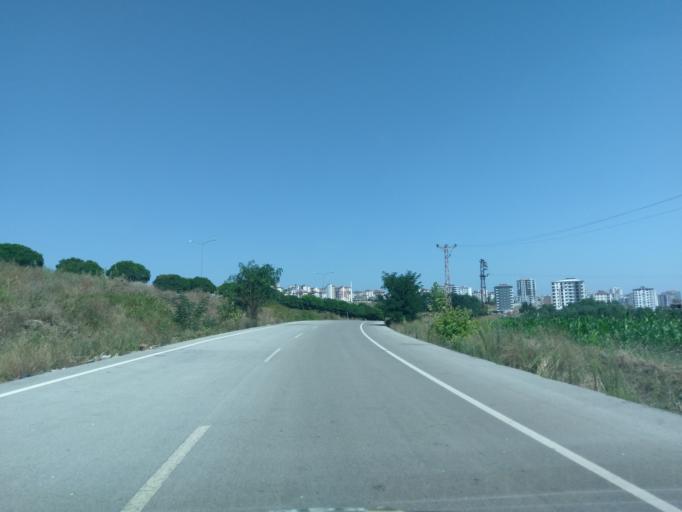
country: TR
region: Samsun
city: Samsun
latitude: 41.2579
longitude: 36.3067
